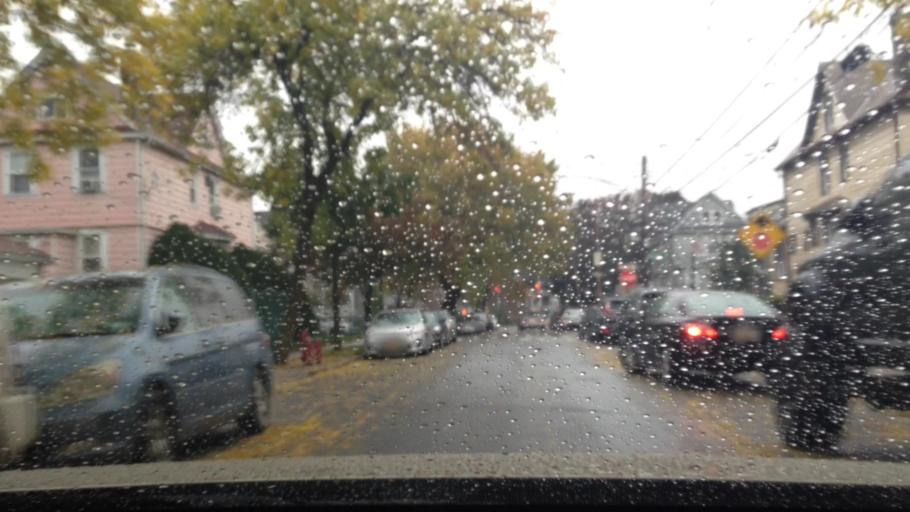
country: US
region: New York
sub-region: Queens County
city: Long Island City
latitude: 40.7393
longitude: -73.8805
